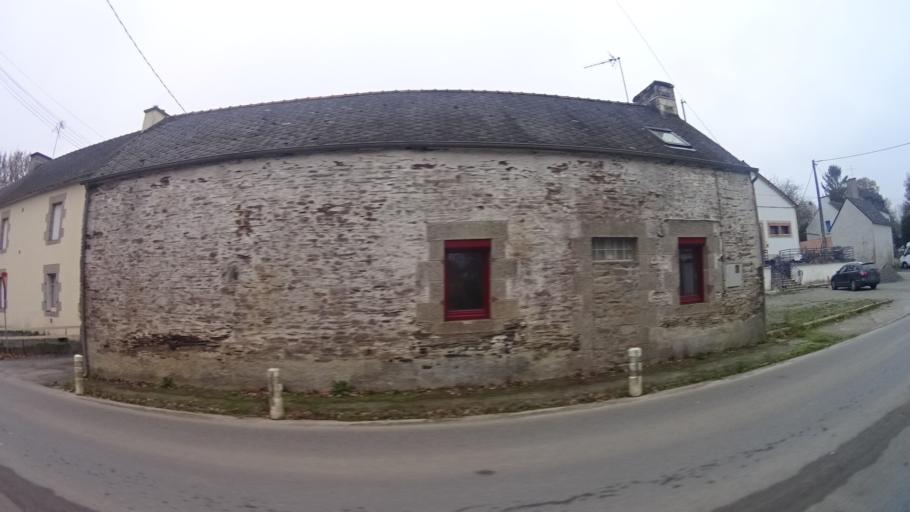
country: FR
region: Brittany
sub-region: Departement du Morbihan
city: Saint-Perreux
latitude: 47.6766
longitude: -2.1081
